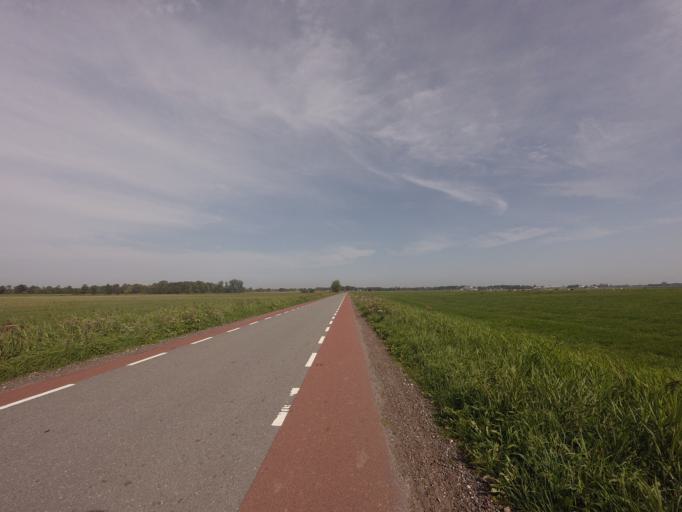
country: NL
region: Groningen
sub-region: Gemeente Leek
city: Leek
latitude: 53.2099
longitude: 6.3463
